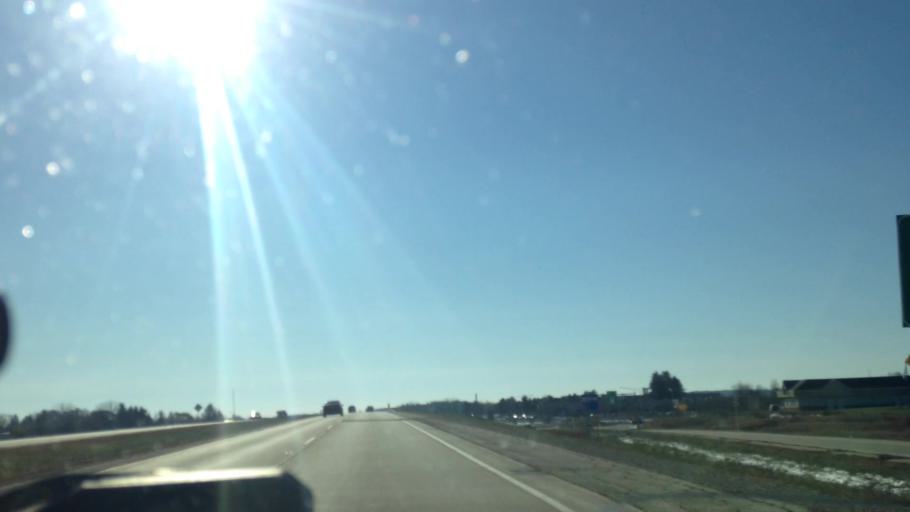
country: US
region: Wisconsin
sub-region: Washington County
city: Jackson
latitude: 43.3273
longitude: -88.1878
